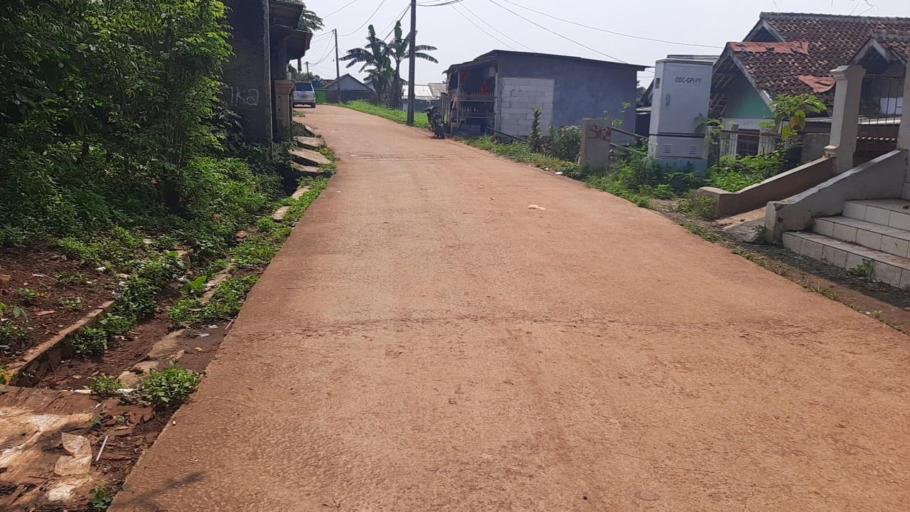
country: ID
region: West Java
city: Cileungsir
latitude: -6.4213
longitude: 106.9135
